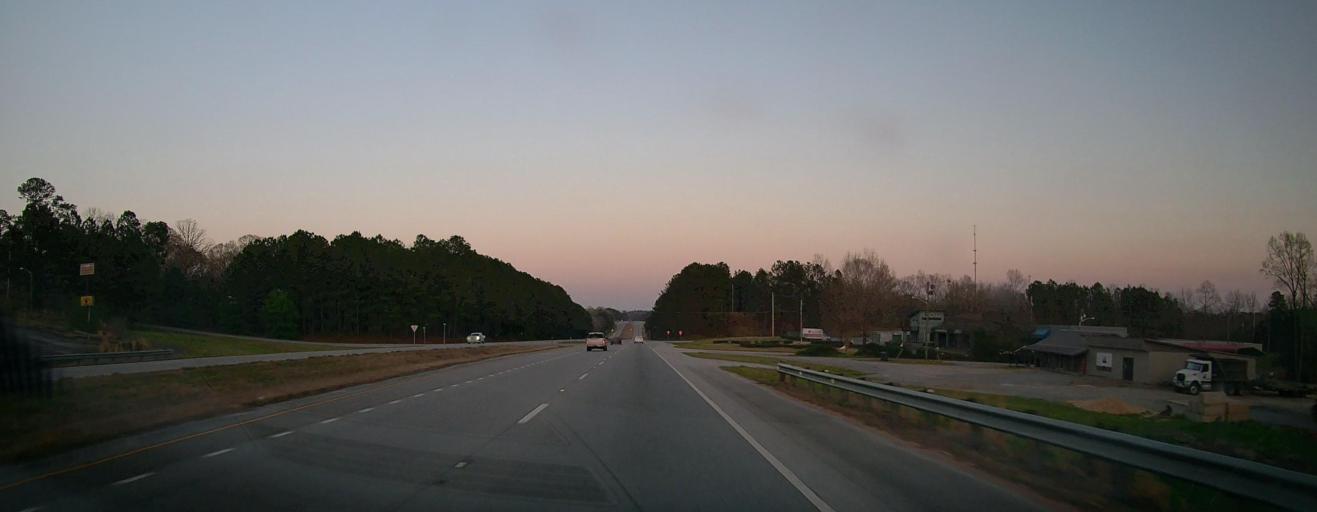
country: US
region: Alabama
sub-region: Tallapoosa County
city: Alexander City
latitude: 32.9067
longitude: -85.9224
